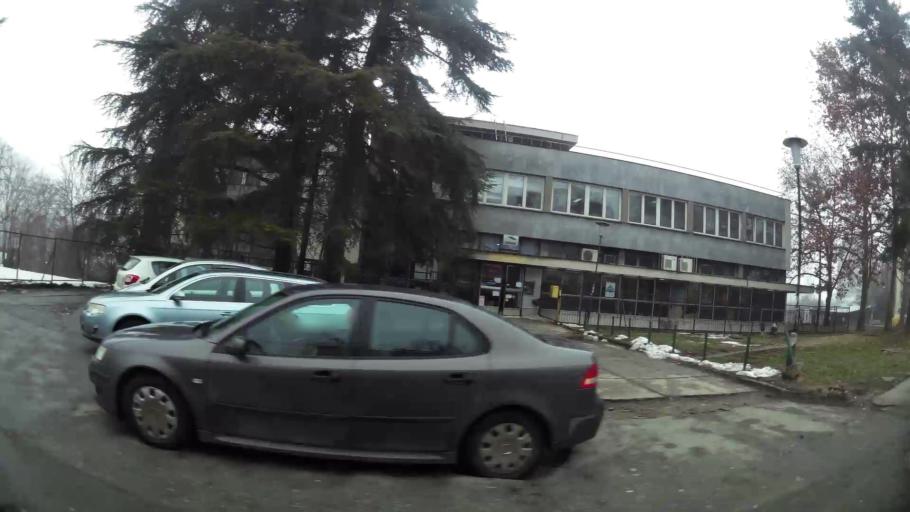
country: RS
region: Central Serbia
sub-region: Belgrade
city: Vozdovac
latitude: 44.7723
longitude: 20.4823
